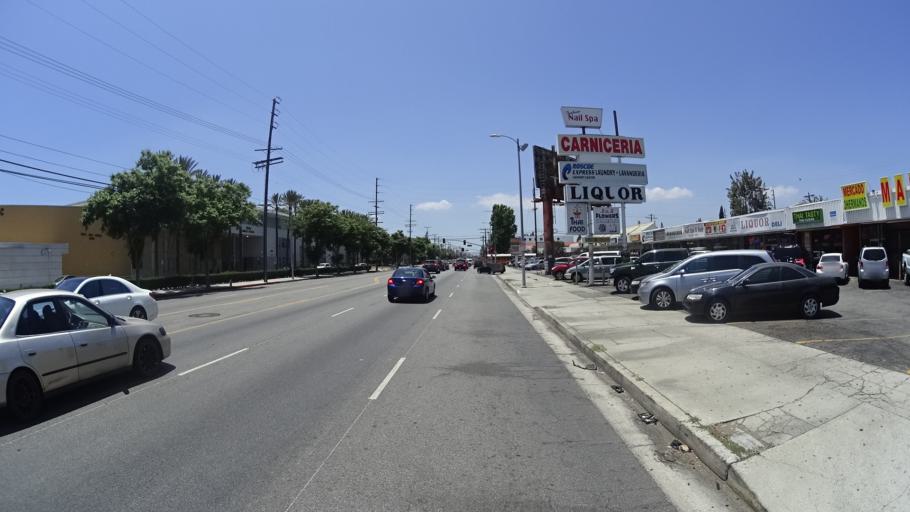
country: US
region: California
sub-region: Los Angeles County
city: Van Nuys
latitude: 34.2216
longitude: -118.4600
